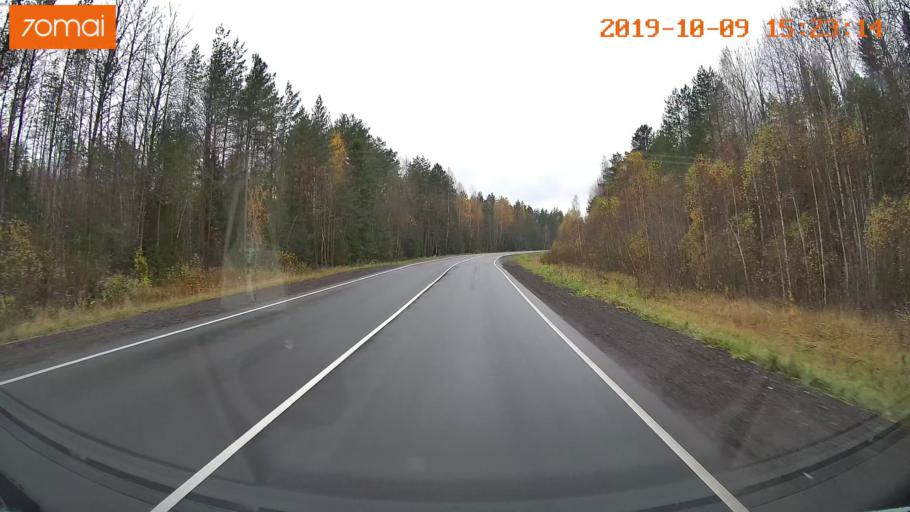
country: RU
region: Kostroma
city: Susanino
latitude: 58.0365
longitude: 41.4849
